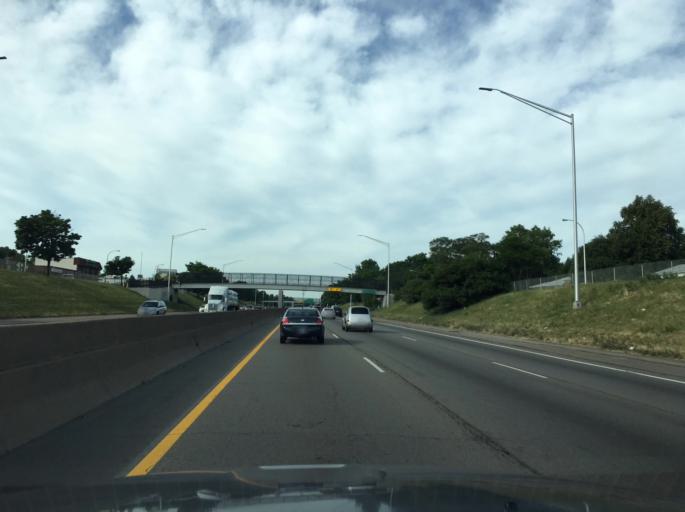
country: US
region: Michigan
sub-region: Wayne County
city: Harper Woods
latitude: 42.4393
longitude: -82.9200
